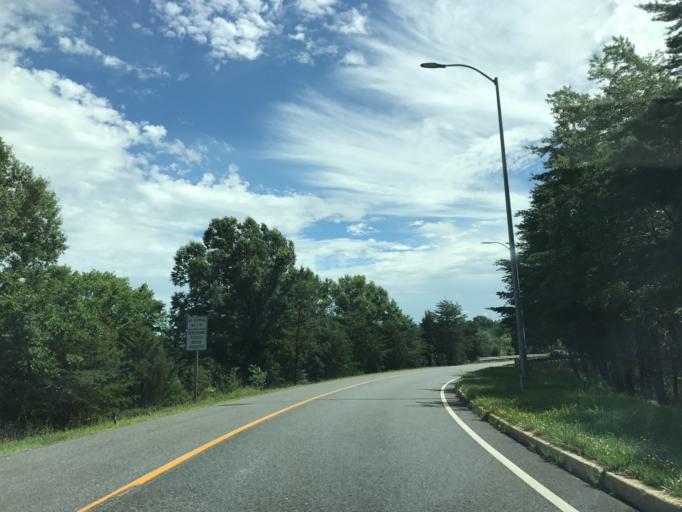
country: US
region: Maryland
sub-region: Howard County
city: North Laurel
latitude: 39.1275
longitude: -76.8612
